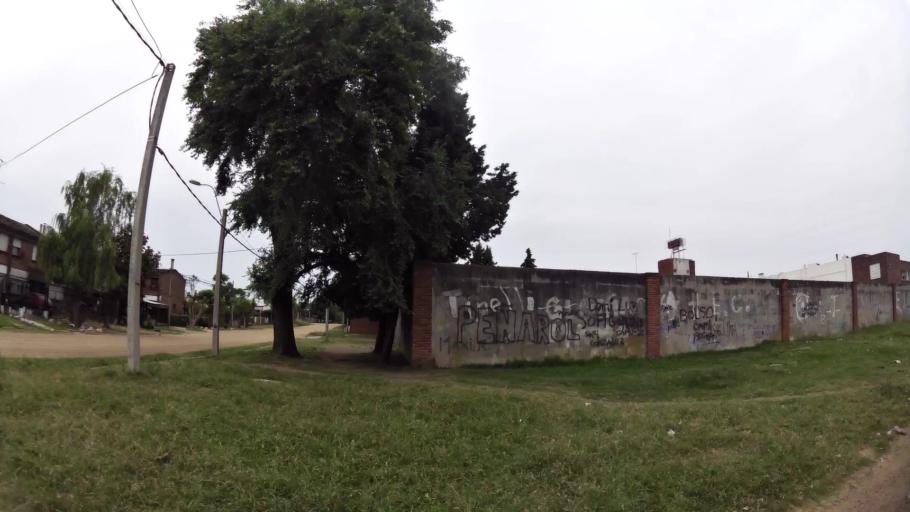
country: UY
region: Canelones
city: La Paz
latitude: -34.7511
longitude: -56.2258
